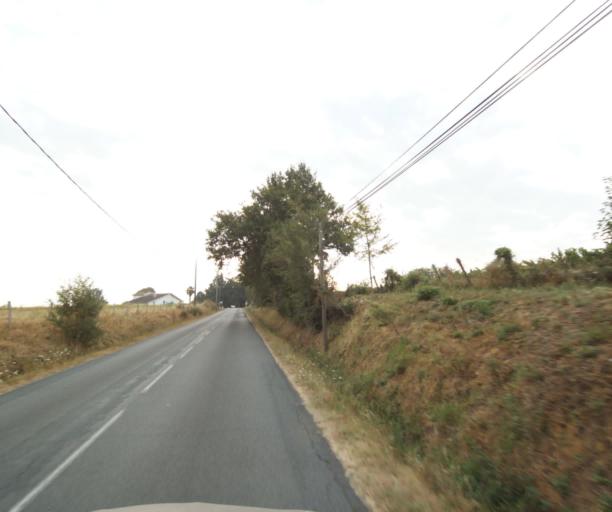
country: FR
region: Aquitaine
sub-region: Departement de la Gironde
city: Creon
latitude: 44.7780
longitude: -0.3411
